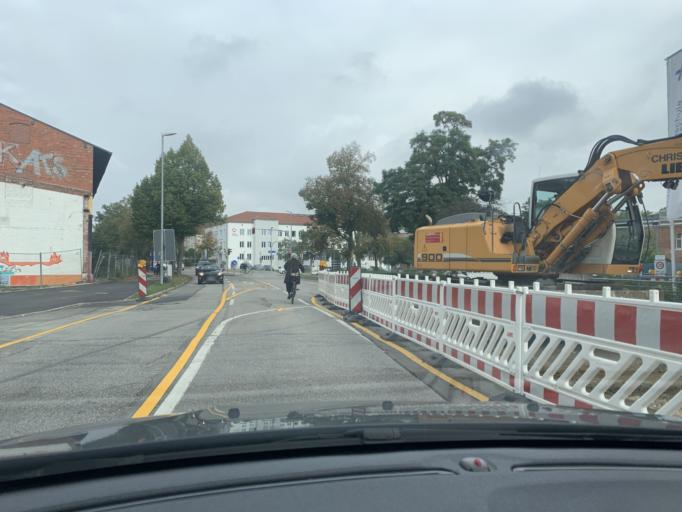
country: DE
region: Bavaria
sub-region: Upper Bavaria
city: Ingolstadt
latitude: 48.7672
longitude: 11.4314
